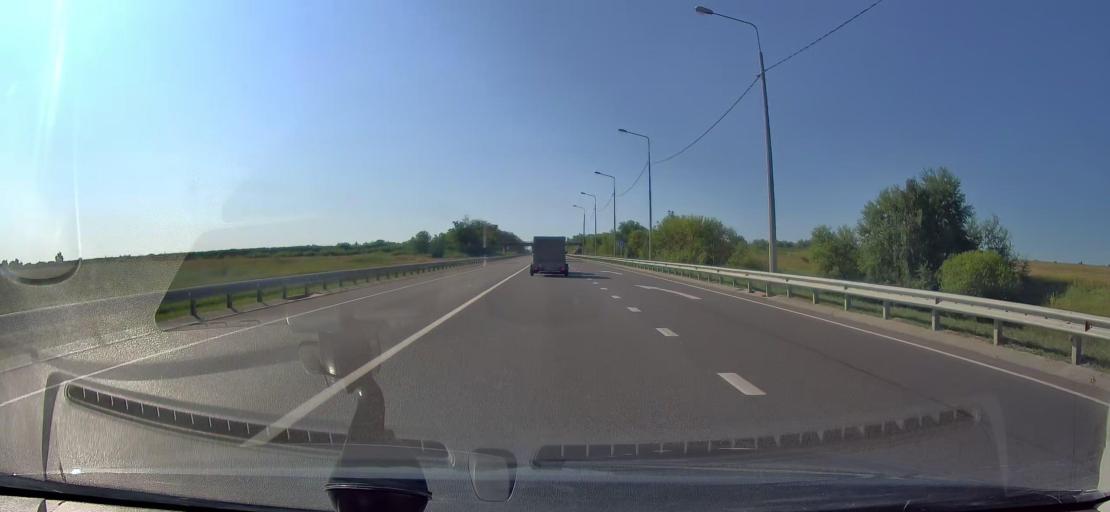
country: RU
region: Orjol
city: Kromy
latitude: 52.6375
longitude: 35.7498
